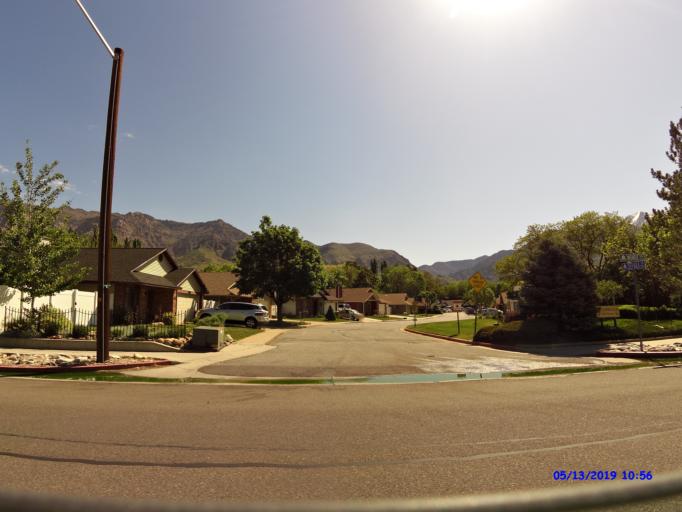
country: US
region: Utah
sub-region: Weber County
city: Ogden
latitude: 41.2426
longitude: -111.9530
